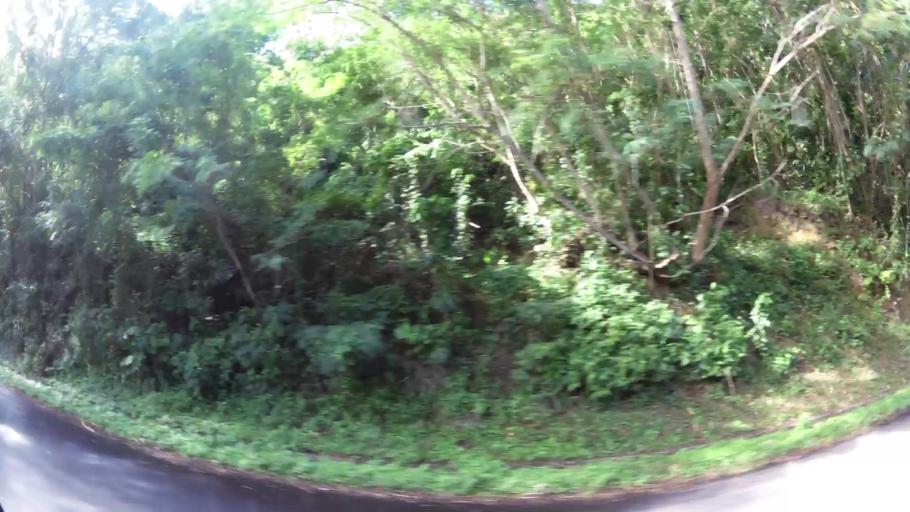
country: LC
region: Soufriere
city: Soufriere
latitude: 13.8300
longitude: -61.0502
